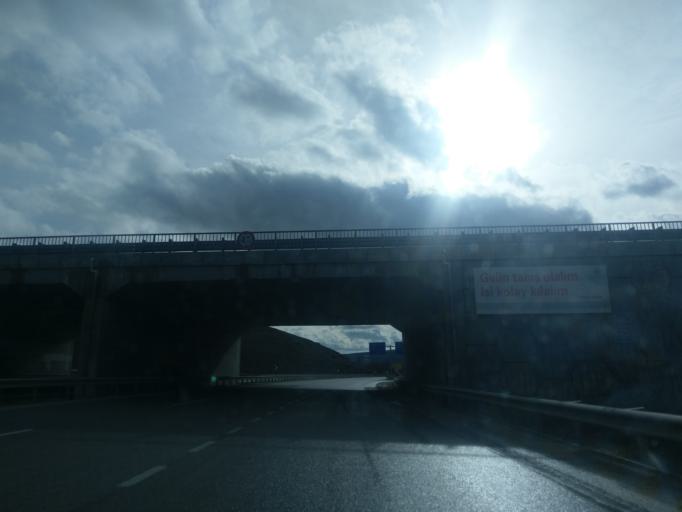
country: TR
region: Eskisehir
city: Inonu
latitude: 39.7092
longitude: 30.1574
